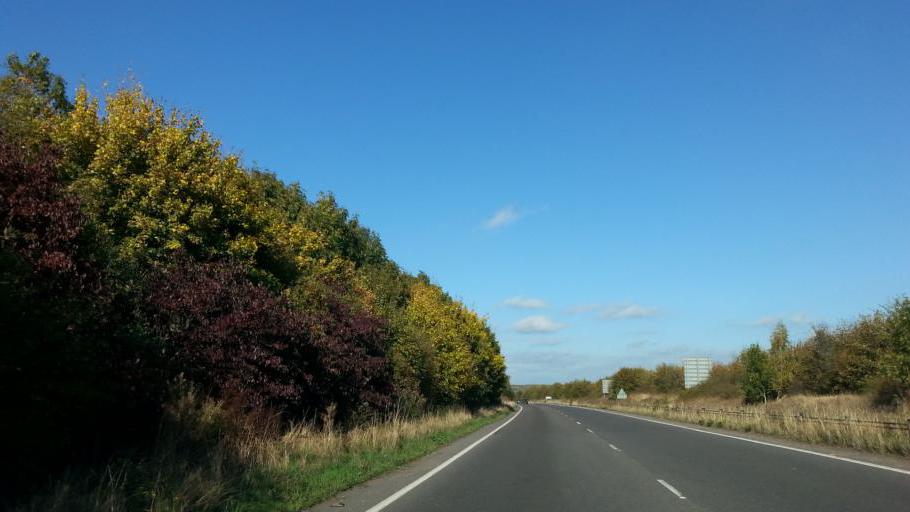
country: GB
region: England
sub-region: Northamptonshire
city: Higham Ferrers
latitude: 52.3102
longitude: -0.5859
